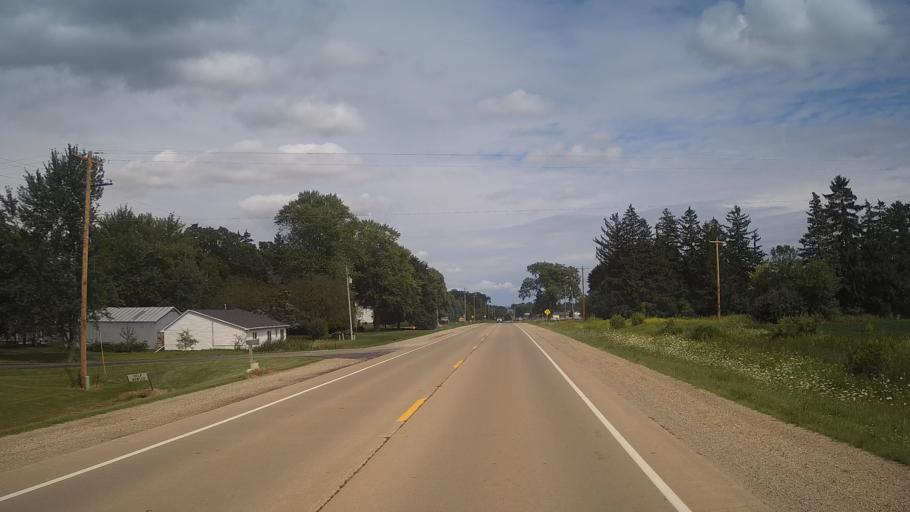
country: US
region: Wisconsin
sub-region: Winnebago County
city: Oshkosh
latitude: 44.0330
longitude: -88.6321
